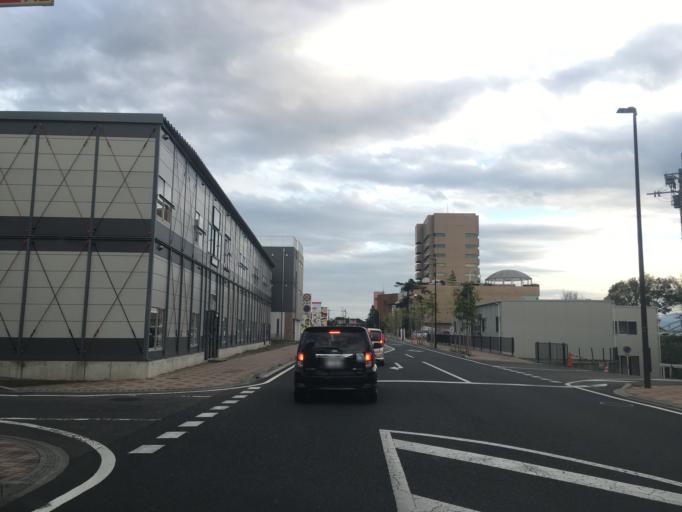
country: JP
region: Gunma
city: Maebashi-shi
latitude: 36.3895
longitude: 139.0595
